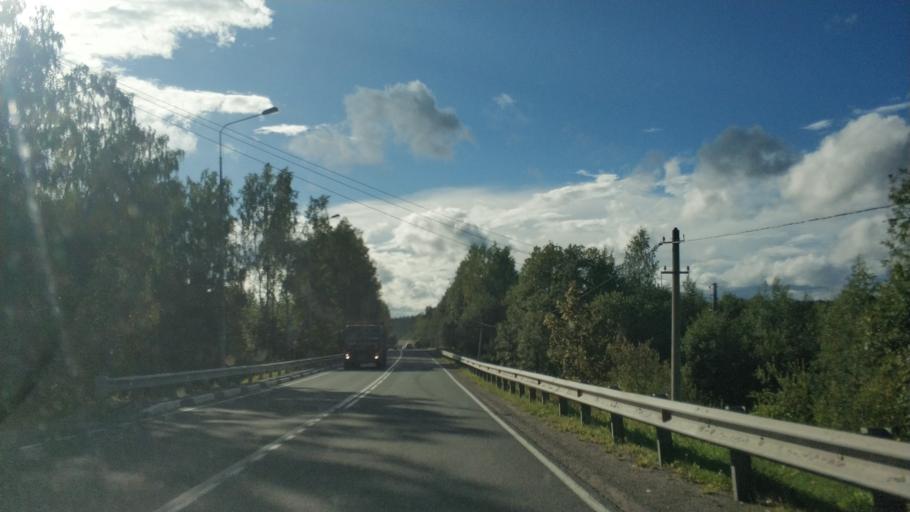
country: RU
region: Republic of Karelia
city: Lakhdenpokh'ya
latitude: 61.5230
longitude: 30.1752
